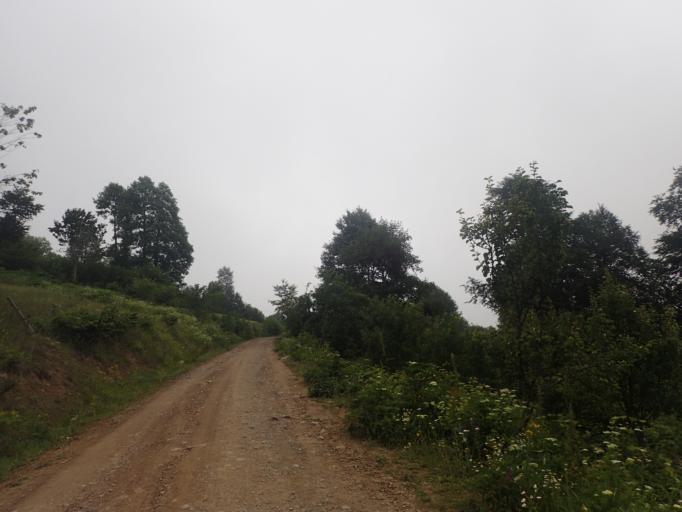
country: TR
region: Ordu
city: Akkus
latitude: 40.8464
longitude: 37.0046
